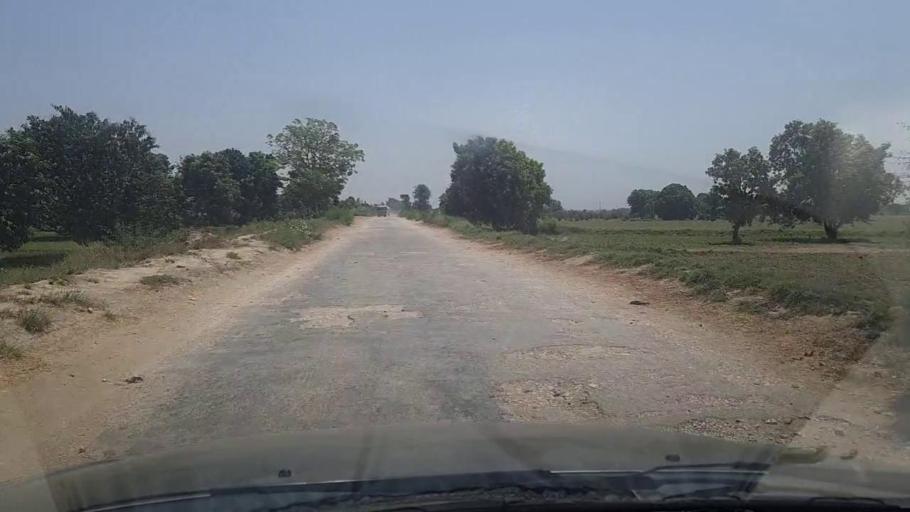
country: PK
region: Sindh
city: Tando Muhammad Khan
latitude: 25.2745
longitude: 68.6246
